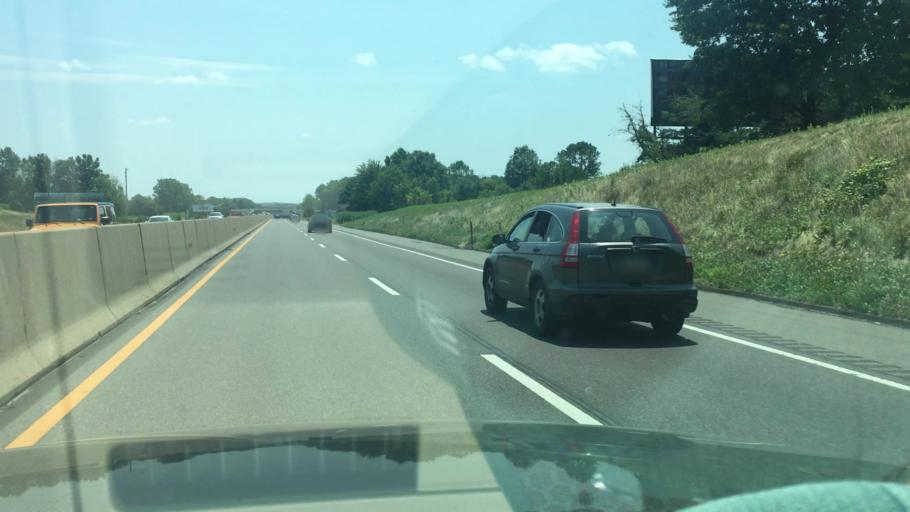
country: US
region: Pennsylvania
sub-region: Bucks County
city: Spinnerstown
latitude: 40.4513
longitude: -75.4370
